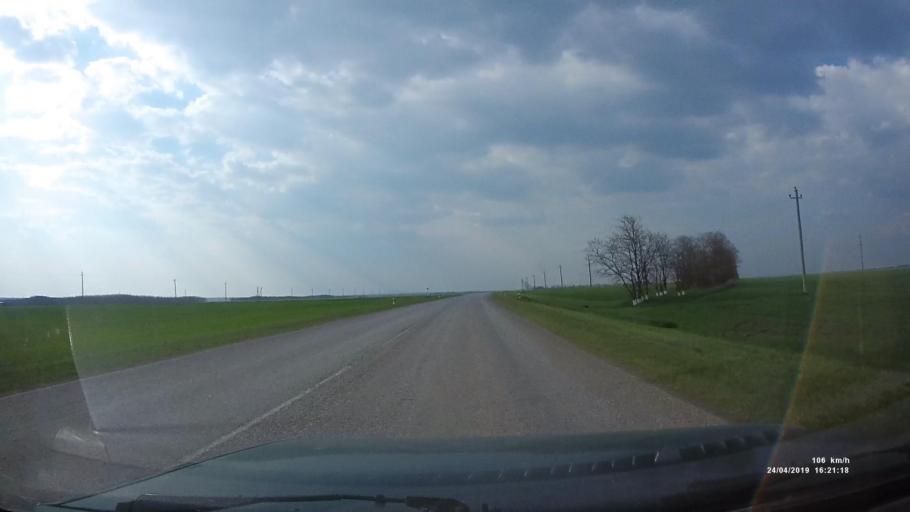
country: RU
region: Rostov
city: Orlovskiy
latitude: 46.8028
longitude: 42.0671
